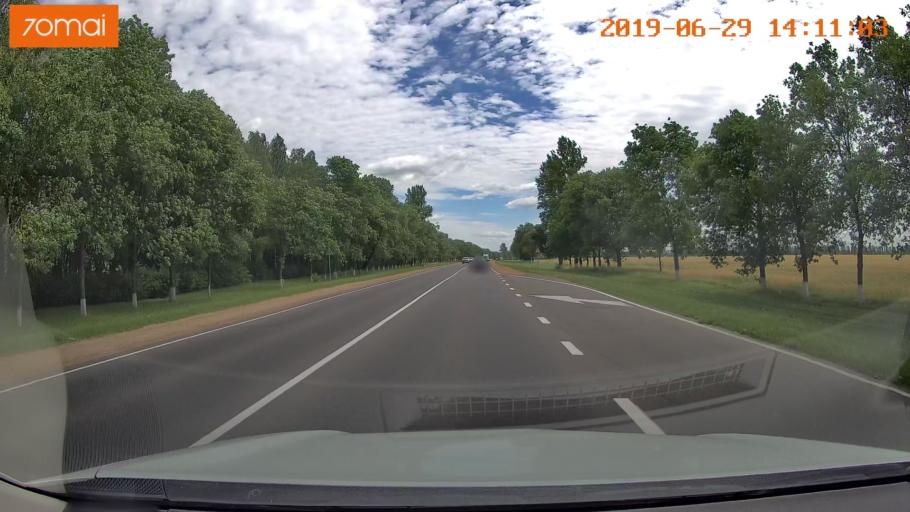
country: BY
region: Minsk
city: Salihorsk
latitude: 52.8235
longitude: 27.4999
